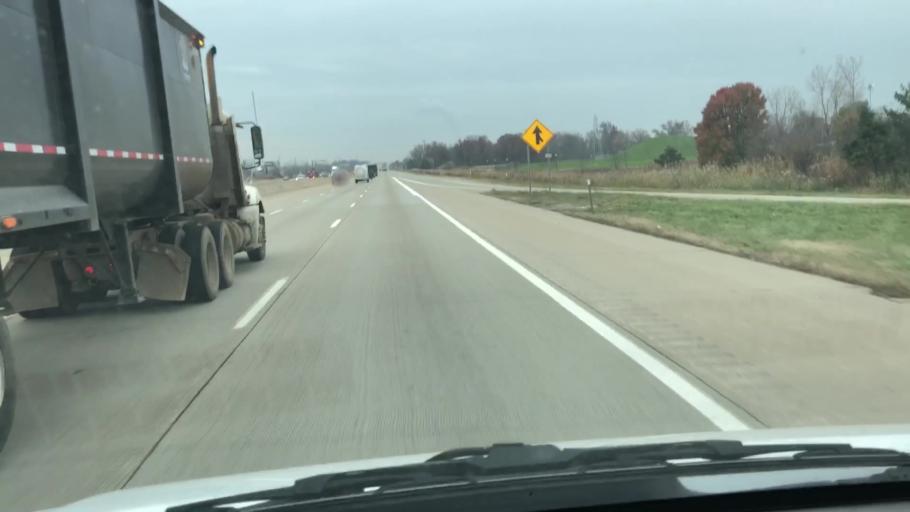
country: US
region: Michigan
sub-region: Wayne County
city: Woodhaven
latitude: 42.1357
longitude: -83.2417
